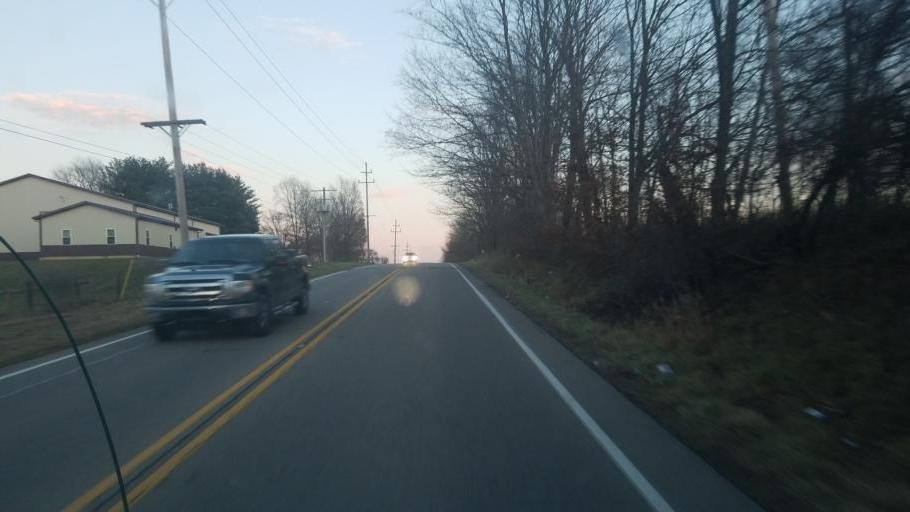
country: US
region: Indiana
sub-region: Lawrence County
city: Bedford
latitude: 38.8756
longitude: -86.4031
